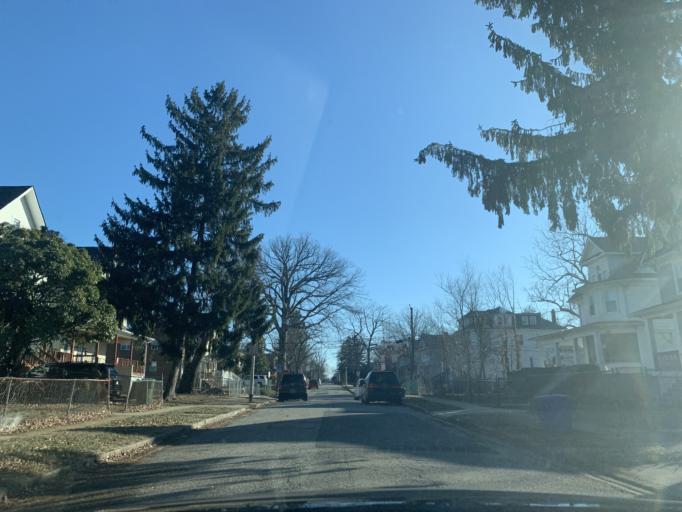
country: US
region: Maryland
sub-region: Baltimore County
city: Lochearn
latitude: 39.3340
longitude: -76.6878
